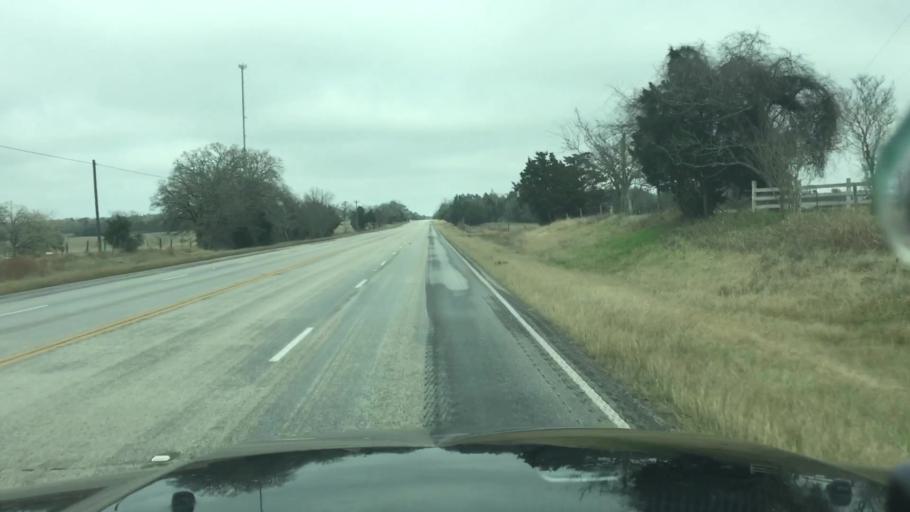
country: US
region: Texas
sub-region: Lee County
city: Giddings
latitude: 30.1047
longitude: -96.9142
